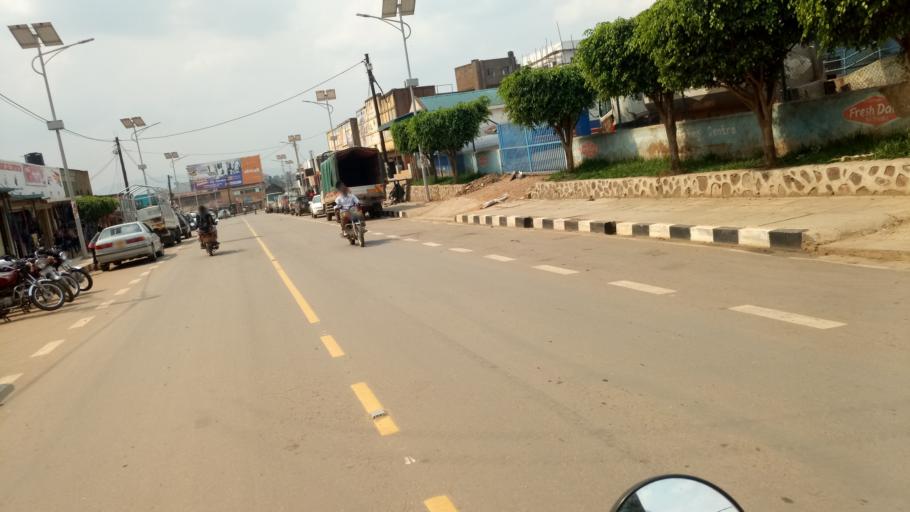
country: UG
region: Western Region
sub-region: Mbarara District
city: Mbarara
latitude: -0.6047
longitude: 30.6617
